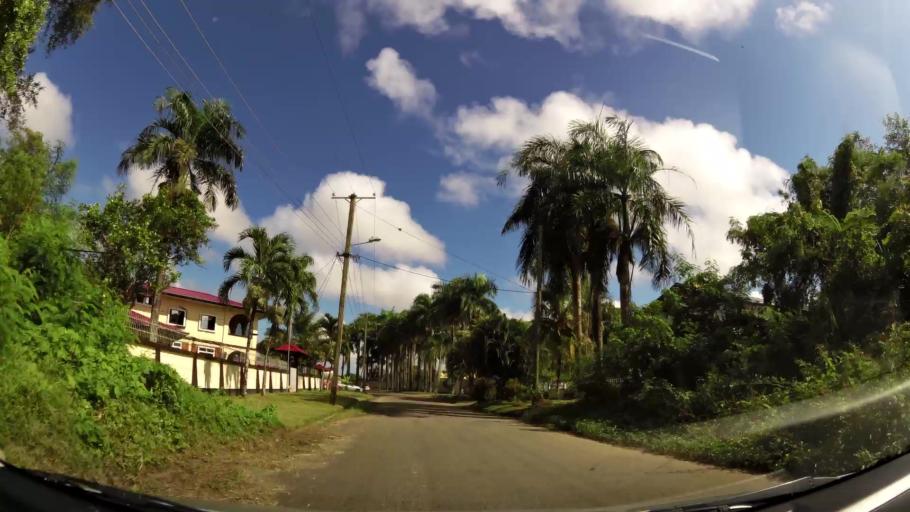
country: SR
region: Commewijne
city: Nieuw Amsterdam
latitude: 5.8734
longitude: -55.1026
